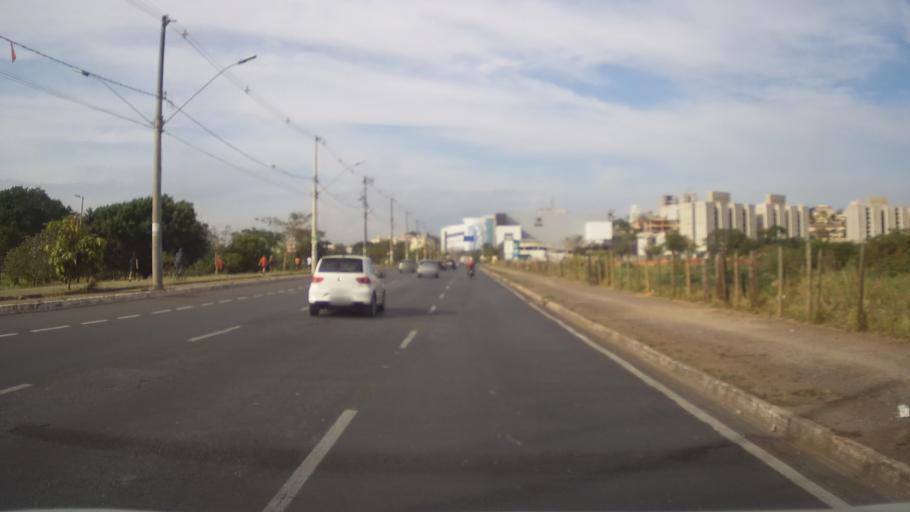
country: BR
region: Minas Gerais
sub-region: Contagem
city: Contagem
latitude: -19.8765
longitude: -44.0344
